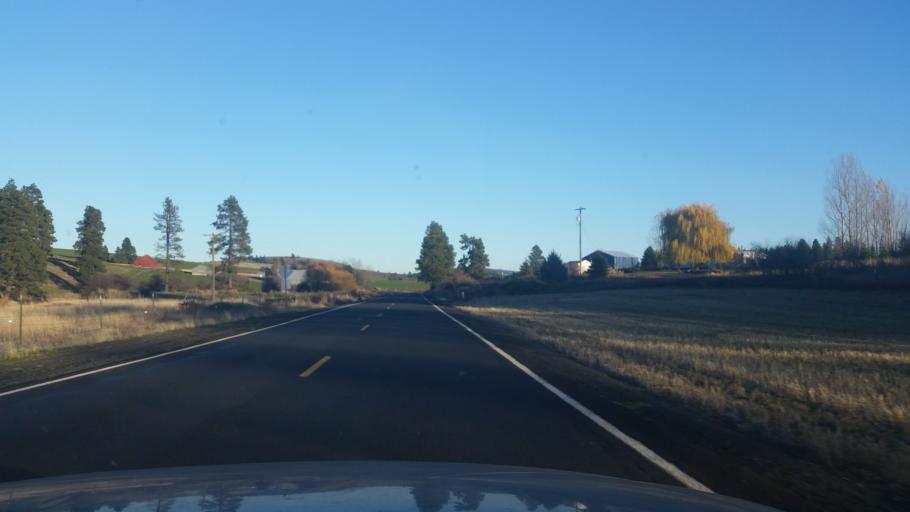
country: US
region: Washington
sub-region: Spokane County
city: Opportunity
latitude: 47.3519
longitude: -117.2521
